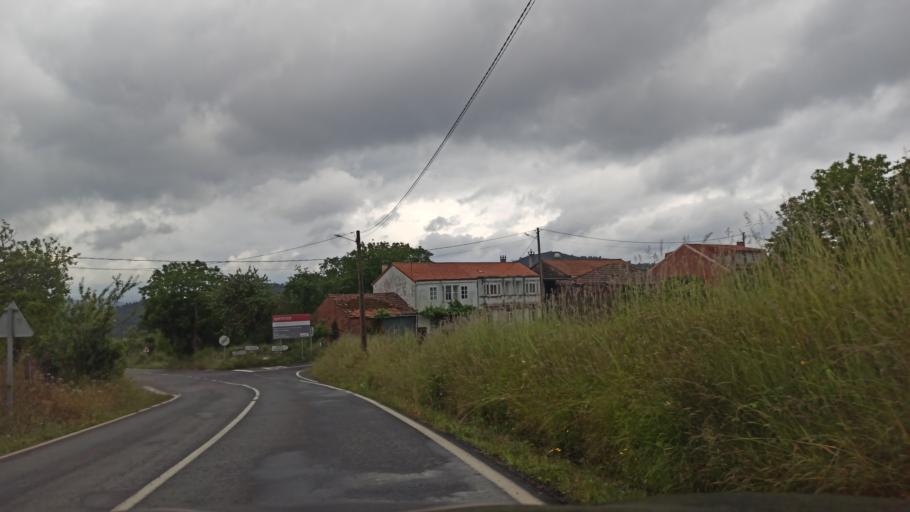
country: ES
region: Galicia
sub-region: Provincia da Coruna
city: Santiso
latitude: 42.7867
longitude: -8.0805
